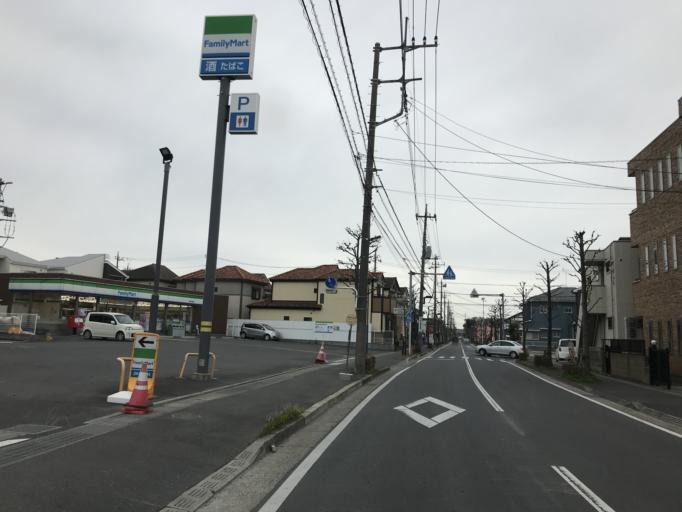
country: JP
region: Saitama
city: Yashio-shi
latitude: 35.8272
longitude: 139.8427
